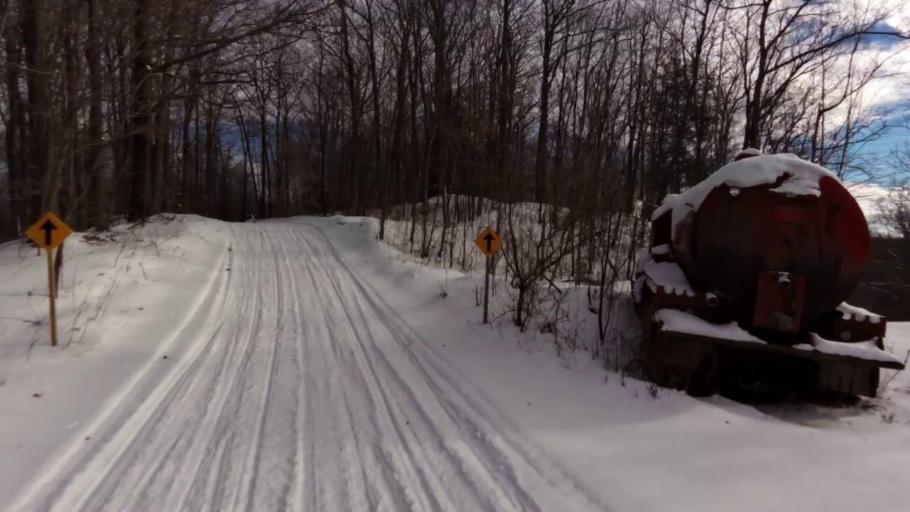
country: US
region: Pennsylvania
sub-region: McKean County
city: Foster Brook
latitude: 42.0037
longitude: -78.5813
